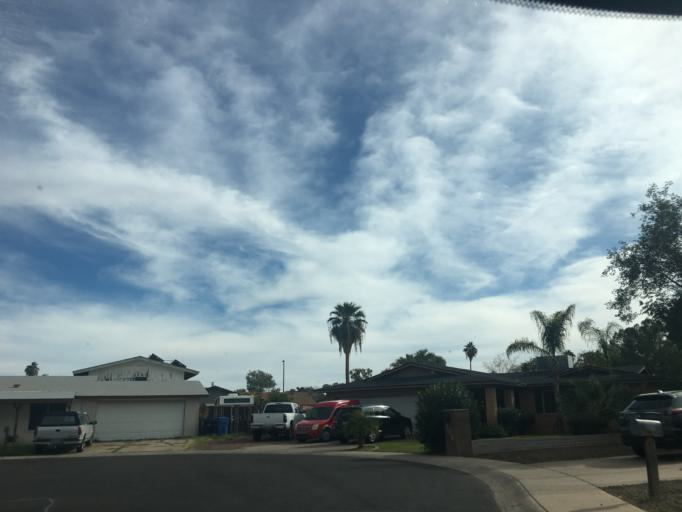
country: US
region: Arizona
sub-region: Maricopa County
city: Gilbert
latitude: 33.3453
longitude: -111.7995
